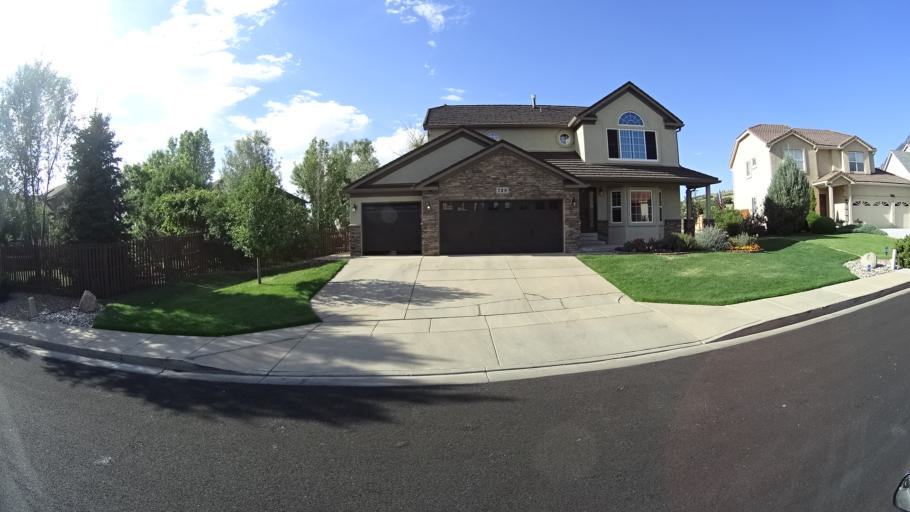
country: US
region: Colorado
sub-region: El Paso County
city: Fort Carson
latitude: 38.7540
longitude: -104.8140
